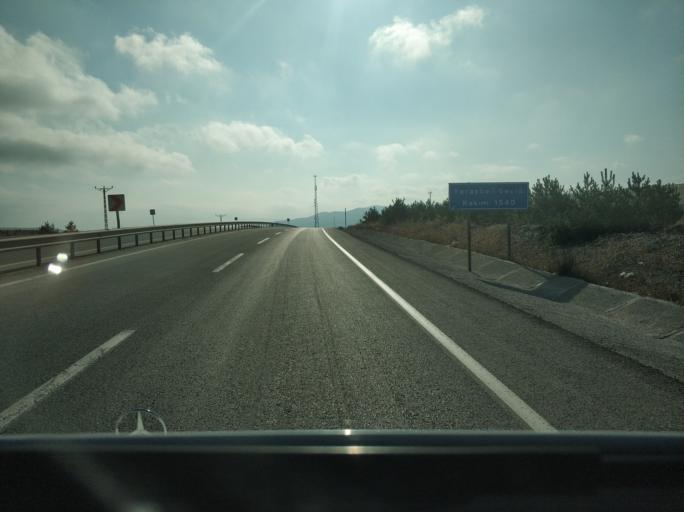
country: TR
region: Sivas
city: Yildizeli
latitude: 39.8352
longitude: 36.4091
